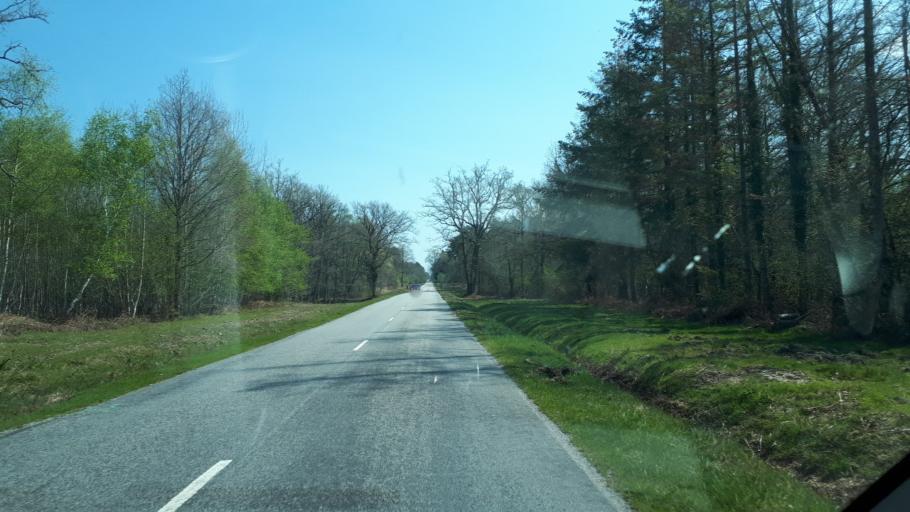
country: FR
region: Centre
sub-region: Departement du Loir-et-Cher
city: Theillay
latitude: 47.3157
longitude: 2.1201
